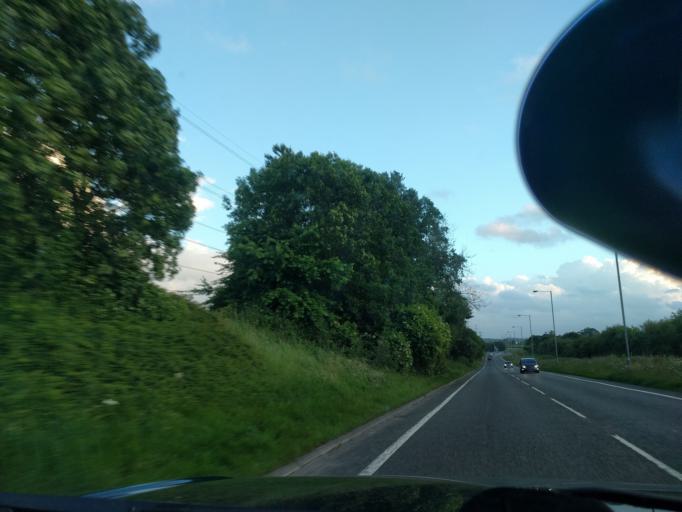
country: GB
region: England
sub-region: Wiltshire
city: Chippenham
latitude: 51.4752
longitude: -2.1357
